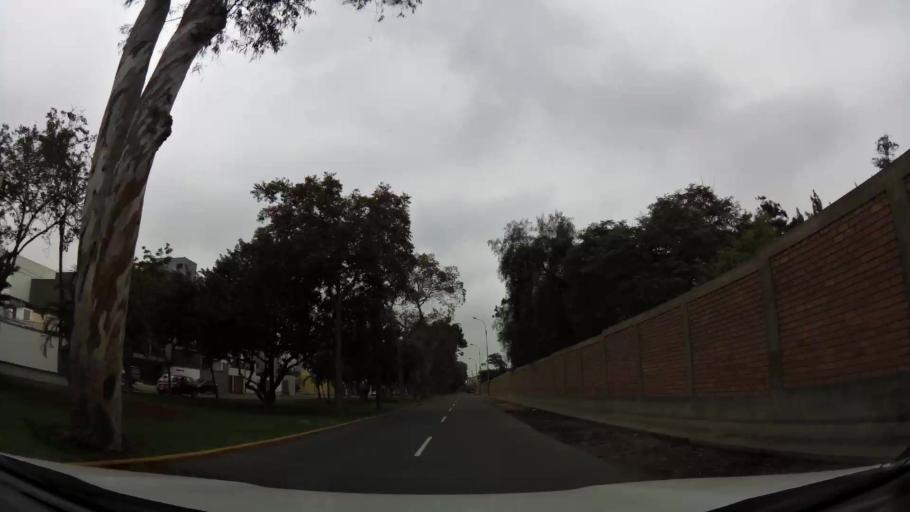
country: PE
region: Lima
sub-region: Lima
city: Surco
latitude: -12.1145
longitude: -76.9875
